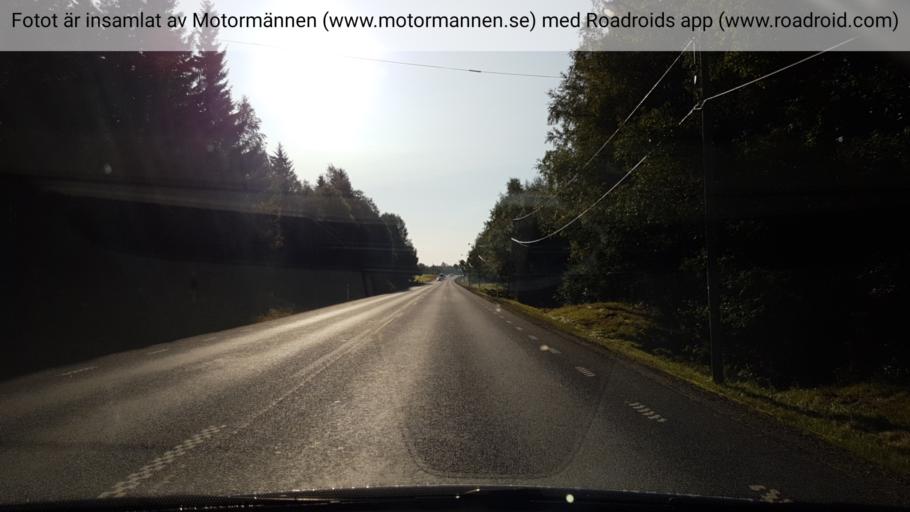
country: SE
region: Vaesterbotten
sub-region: Umea Kommun
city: Roback
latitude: 63.8810
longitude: 20.0457
